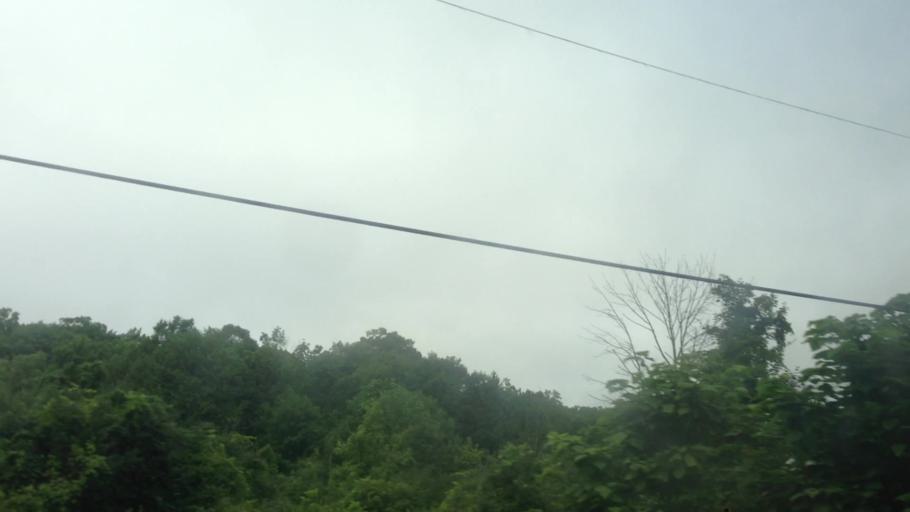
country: US
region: New York
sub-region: Dutchess County
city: Red Hook
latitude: 41.9999
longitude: -73.9133
